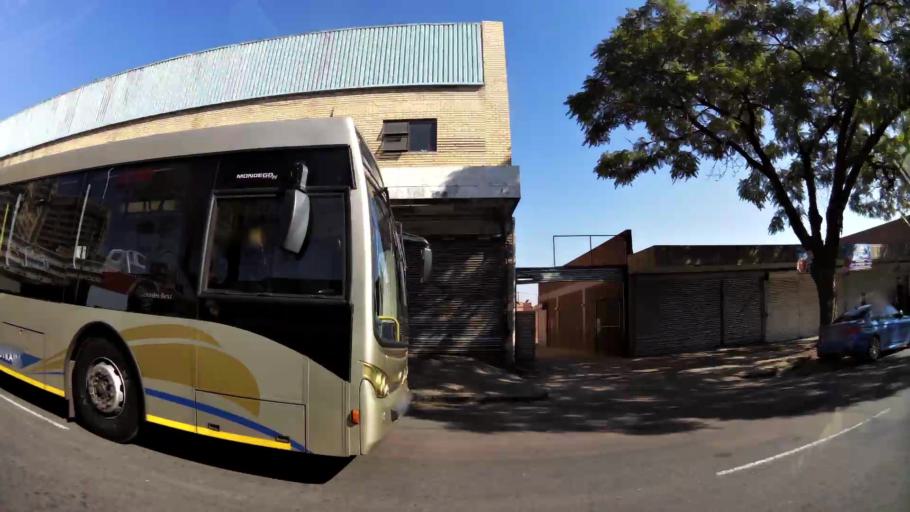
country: ZA
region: Gauteng
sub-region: City of Tshwane Metropolitan Municipality
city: Pretoria
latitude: -25.7416
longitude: 28.1852
